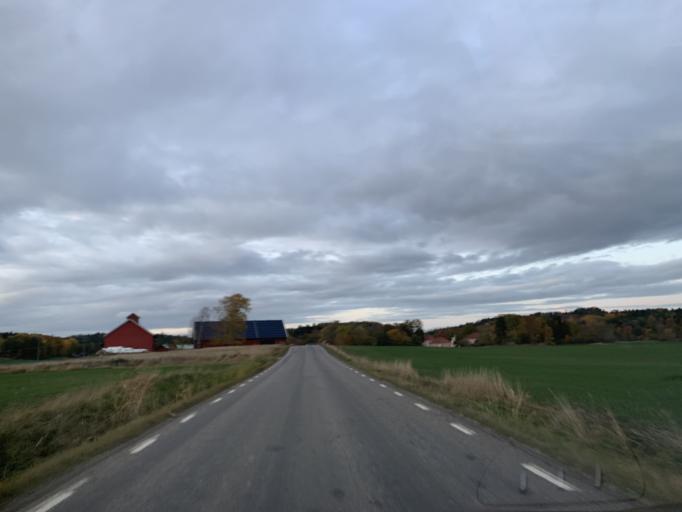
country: SE
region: Stockholm
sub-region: Nynashamns Kommun
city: Osmo
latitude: 58.9546
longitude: 17.7668
